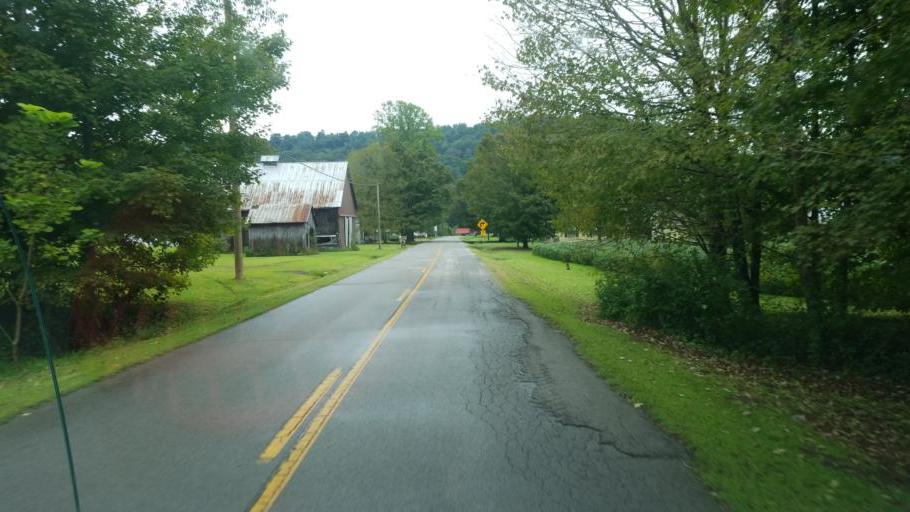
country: US
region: Kentucky
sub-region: Rowan County
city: Morehead
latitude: 38.3525
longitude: -83.5290
